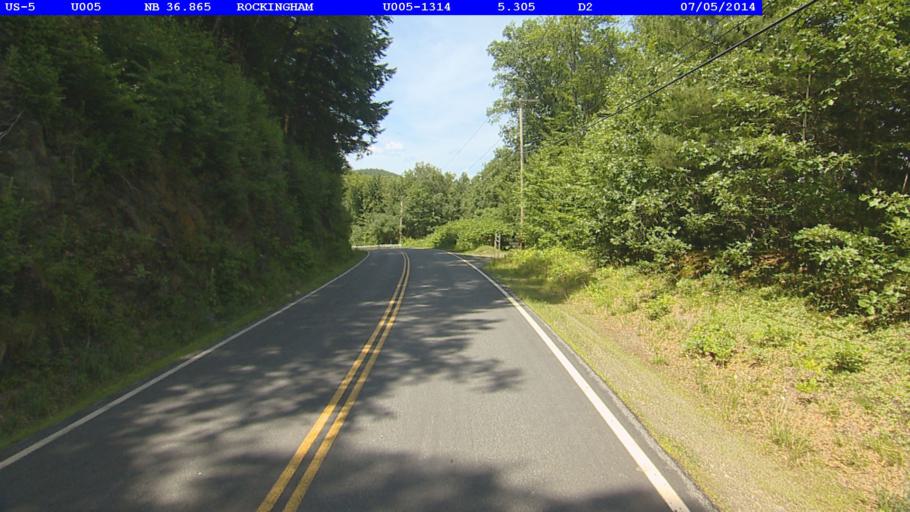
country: US
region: Vermont
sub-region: Windham County
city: Rockingham
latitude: 43.1921
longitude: -72.4508
